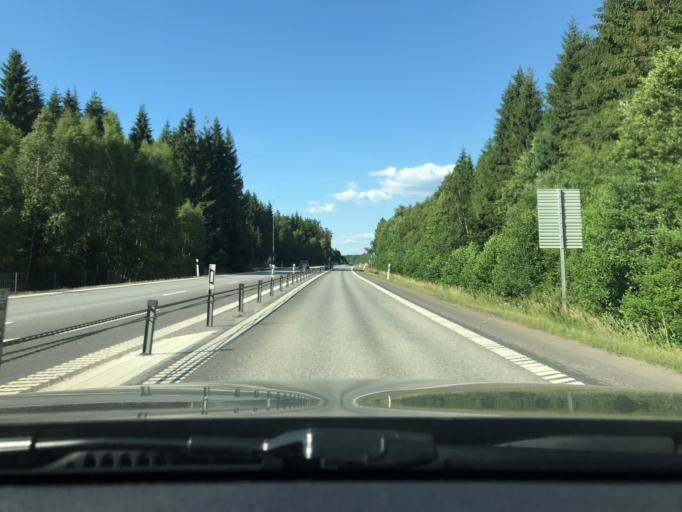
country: SE
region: Skane
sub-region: Osby Kommun
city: Osby
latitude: 56.4050
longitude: 14.0411
